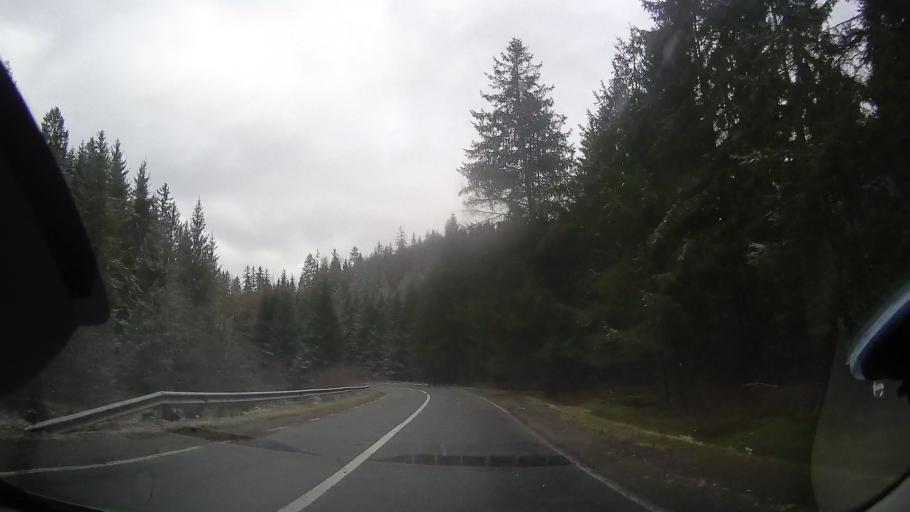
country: RO
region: Cluj
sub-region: Comuna Calatele
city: Calatele
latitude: 46.7436
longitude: 23.0161
